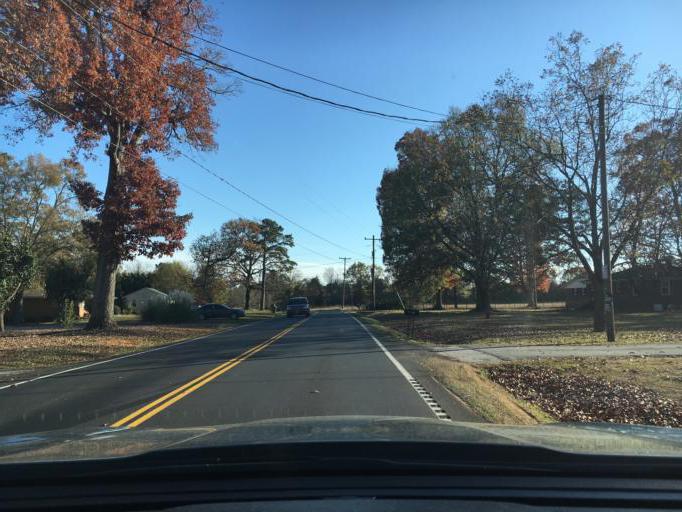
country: US
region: South Carolina
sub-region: Spartanburg County
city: Inman
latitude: 35.0095
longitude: -82.0744
